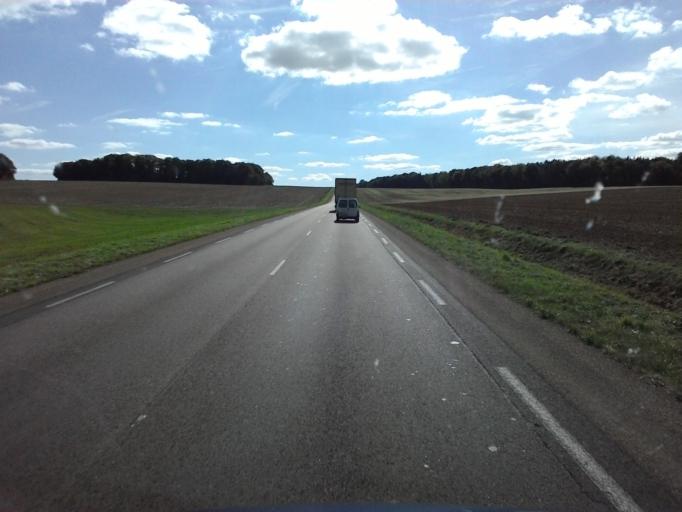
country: FR
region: Bourgogne
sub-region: Departement de la Cote-d'Or
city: Chatillon-sur-Seine
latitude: 47.7911
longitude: 4.5156
